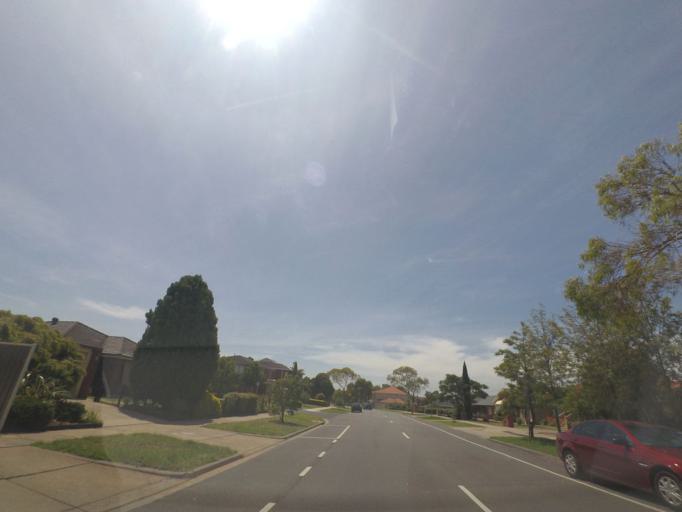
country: AU
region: Victoria
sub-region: Brimbank
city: Keilor Lodge
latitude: -37.7061
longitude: 144.7947
